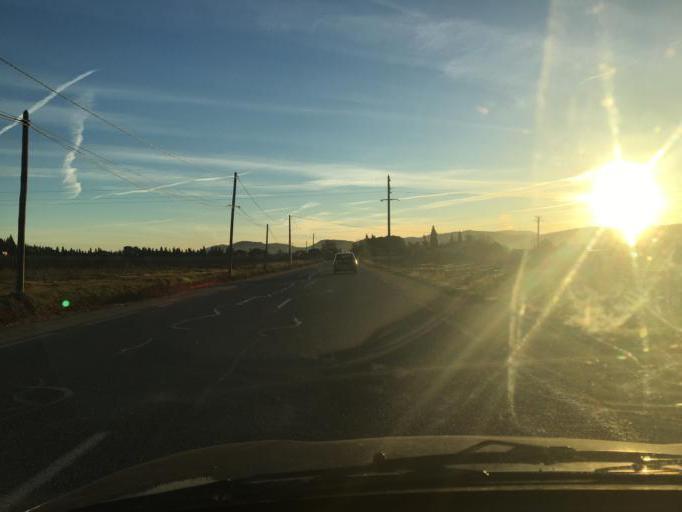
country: FR
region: Provence-Alpes-Cote d'Azur
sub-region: Departement du Var
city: Les Arcs
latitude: 43.4496
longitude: 6.4684
